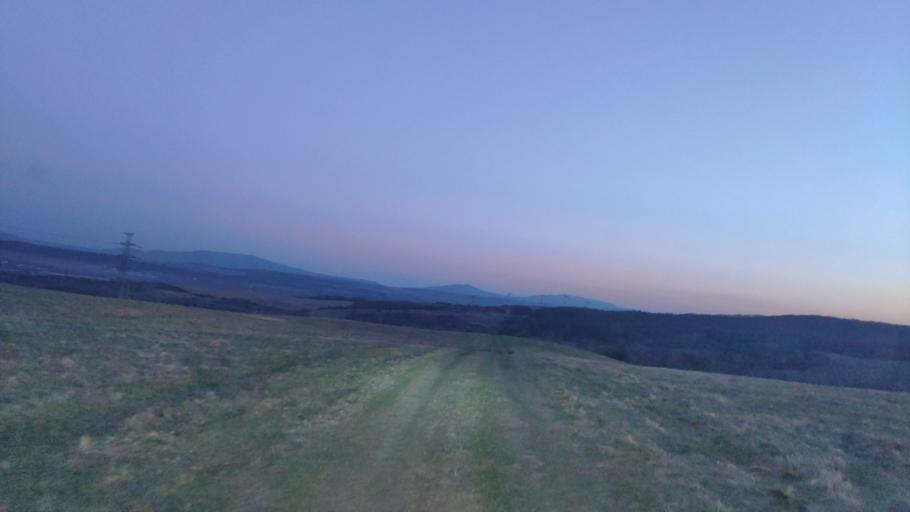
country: SK
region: Kosicky
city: Kosice
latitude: 48.8289
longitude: 21.2619
